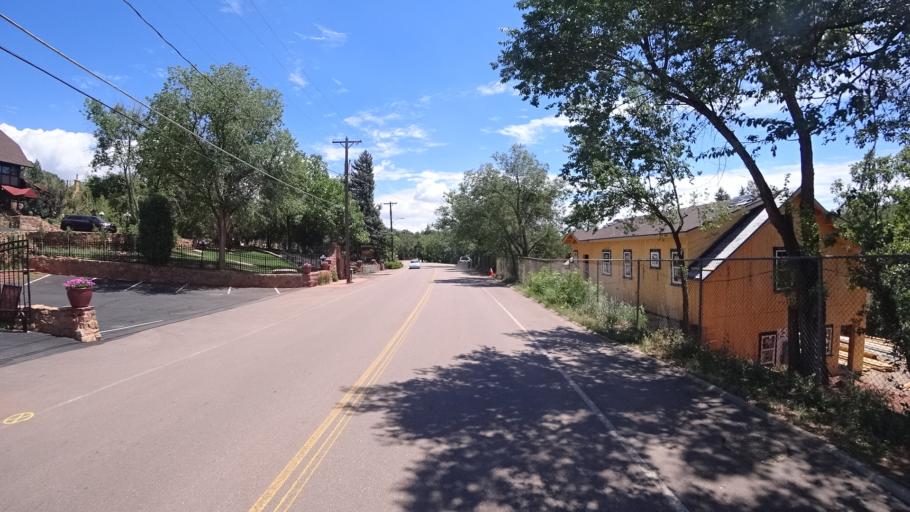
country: US
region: Colorado
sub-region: El Paso County
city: Manitou Springs
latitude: 38.8589
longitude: -104.9029
